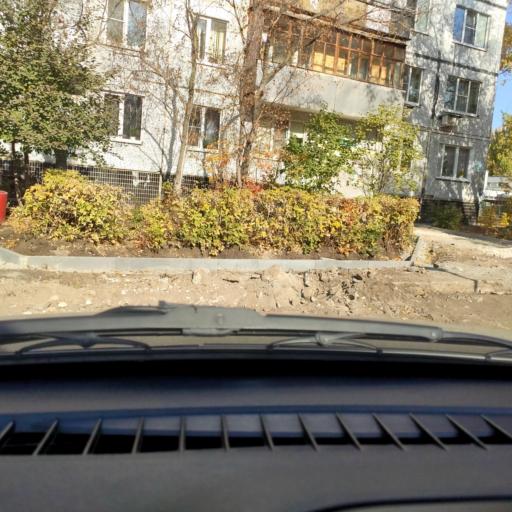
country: RU
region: Samara
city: Tol'yatti
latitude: 53.5119
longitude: 49.2582
